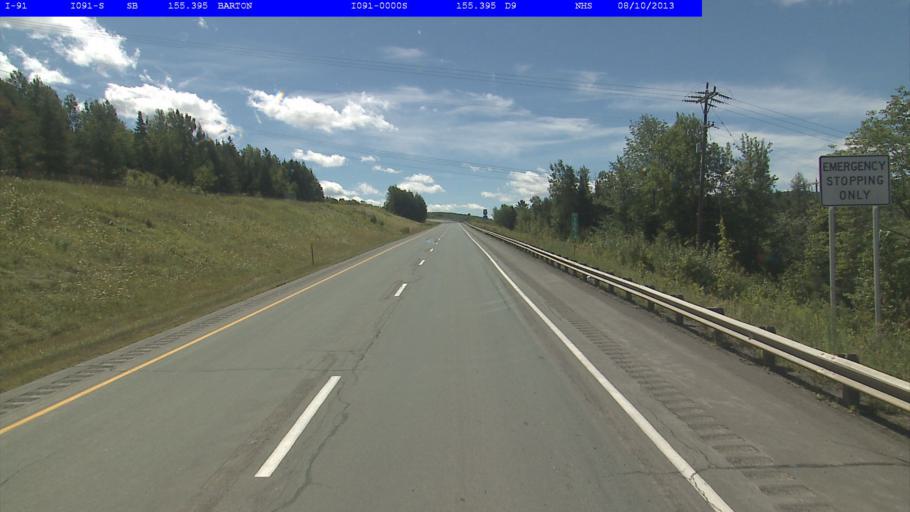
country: US
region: Vermont
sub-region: Orleans County
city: Newport
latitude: 44.7282
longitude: -72.1805
